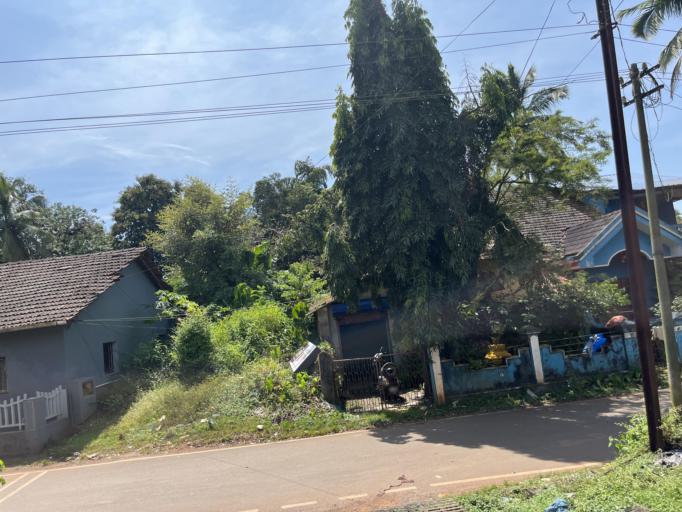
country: IN
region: Goa
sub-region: North Goa
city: Ponda
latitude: 15.3992
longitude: 74.0133
